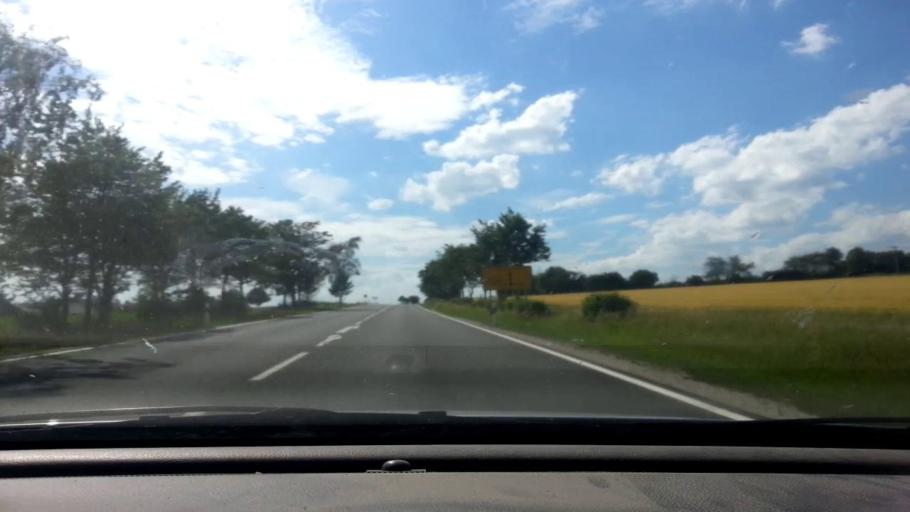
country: DE
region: Bavaria
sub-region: Upper Palatinate
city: Erbendorf
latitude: 49.8509
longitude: 11.9871
